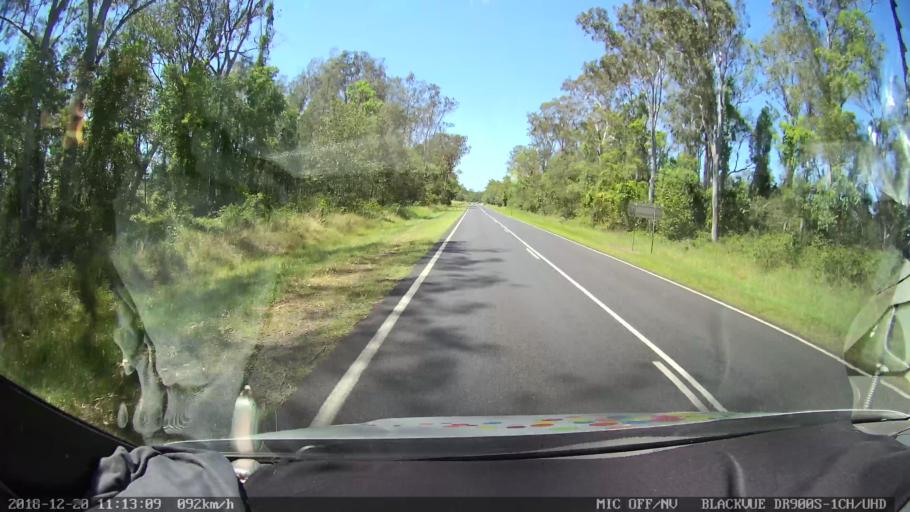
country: AU
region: New South Wales
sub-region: Richmond Valley
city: Casino
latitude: -28.9839
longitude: 153.0096
